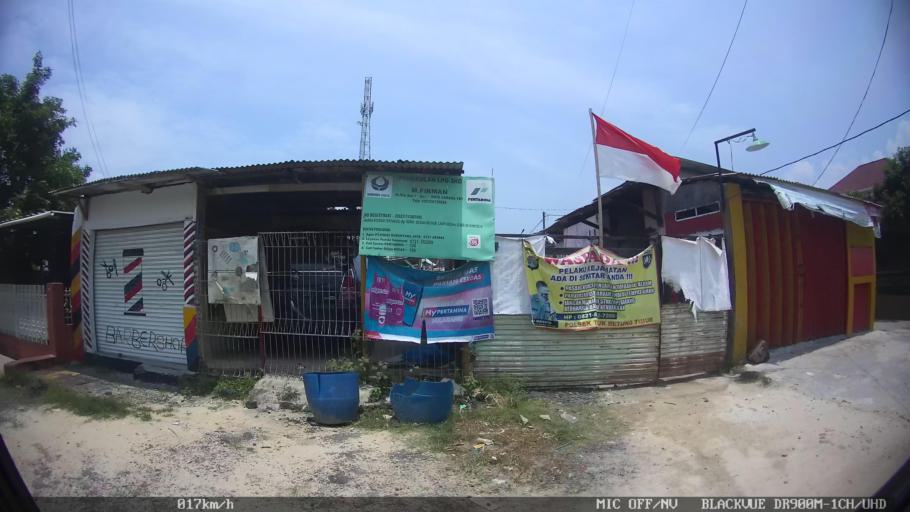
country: ID
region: Lampung
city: Bandarlampung
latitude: -5.4542
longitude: 105.2609
